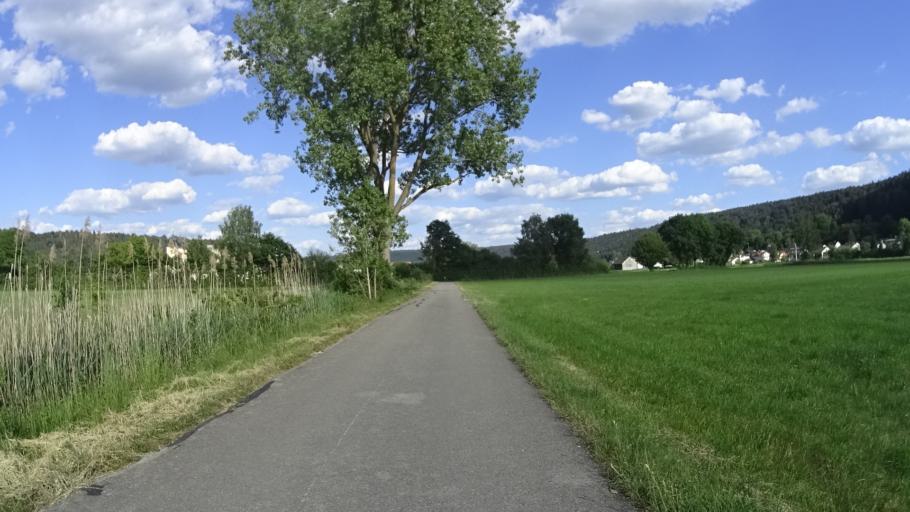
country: DE
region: Bavaria
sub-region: Upper Palatinate
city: Dietfurt
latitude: 49.0197
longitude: 11.5141
